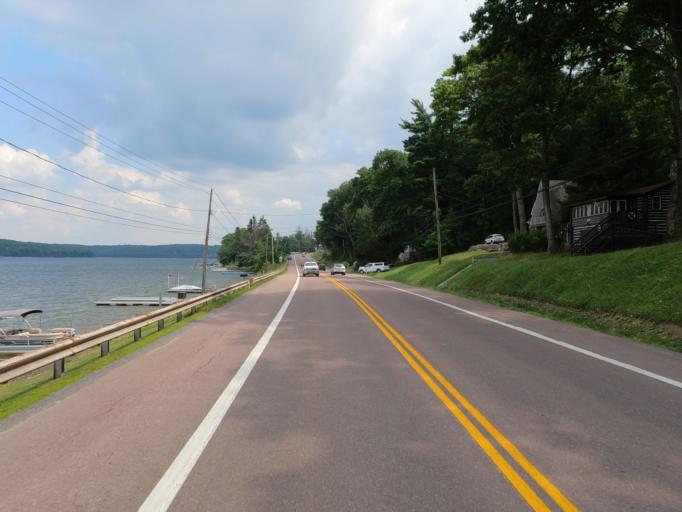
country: US
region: Maryland
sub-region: Garrett County
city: Mountain Lake Park
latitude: 39.5190
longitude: -79.3286
